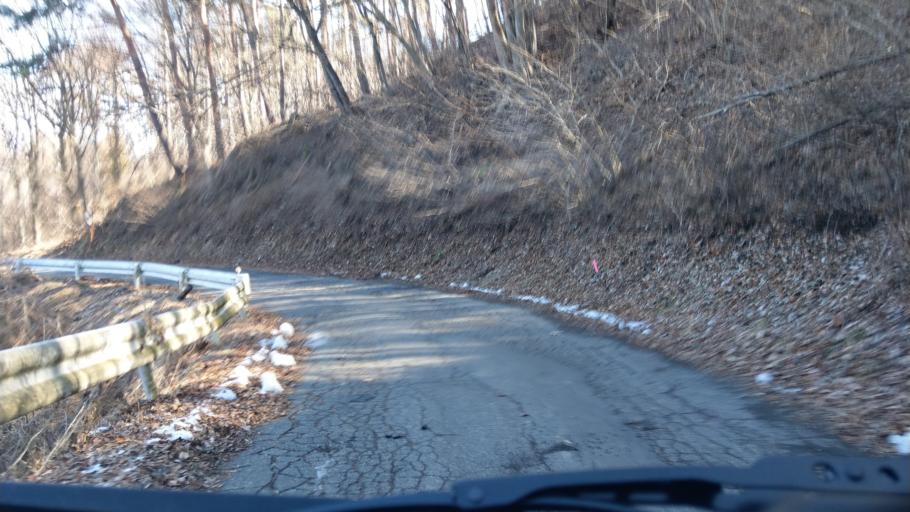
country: JP
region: Nagano
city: Komoro
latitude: 36.3152
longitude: 138.4035
